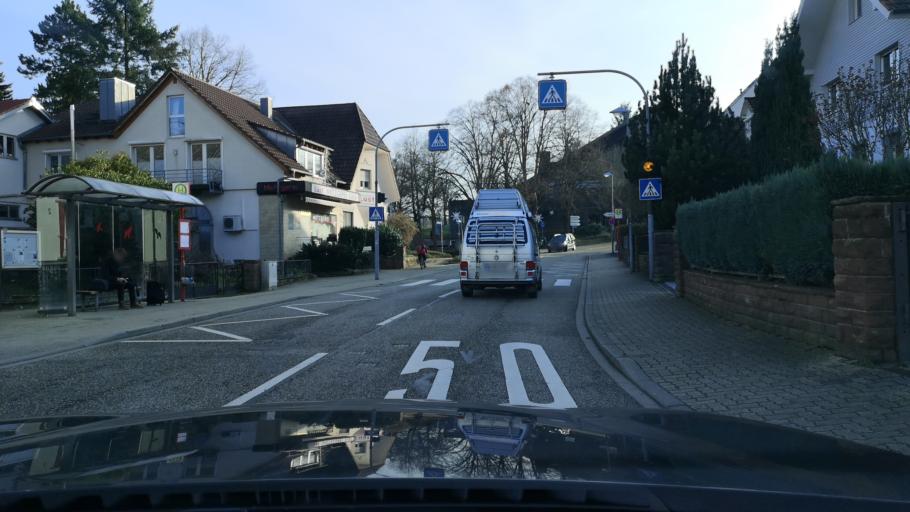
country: DE
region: Baden-Wuerttemberg
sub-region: Karlsruhe Region
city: Ettlingen
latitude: 48.9684
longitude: 8.4782
